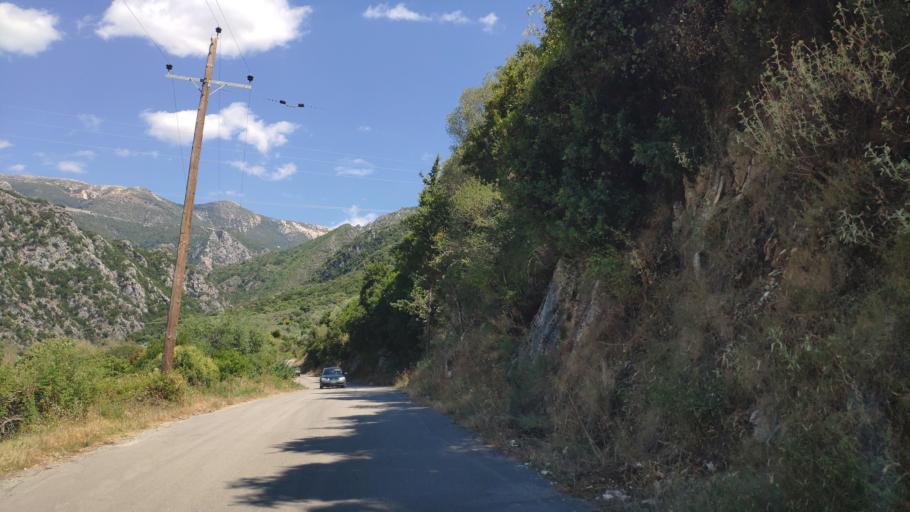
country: GR
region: Epirus
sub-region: Nomos Prevezis
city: Kanalaki
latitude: 39.3254
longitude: 20.6141
